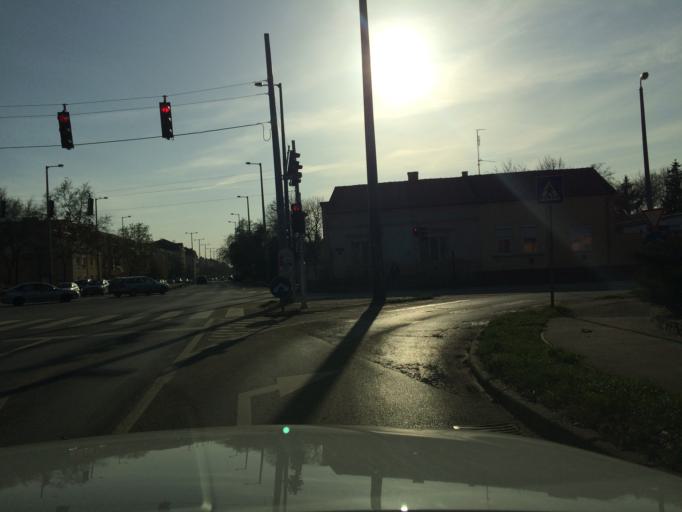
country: HU
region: Szabolcs-Szatmar-Bereg
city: Nyiregyhaza
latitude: 47.9512
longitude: 21.7268
